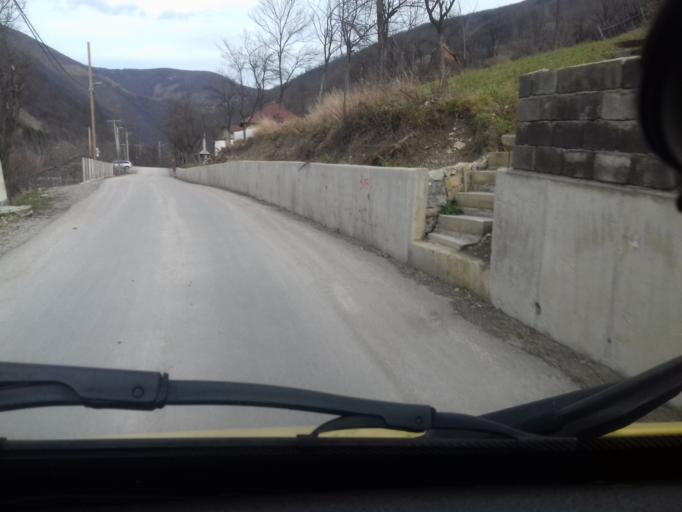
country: BA
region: Federation of Bosnia and Herzegovina
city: Zenica
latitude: 44.2382
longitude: 17.9131
